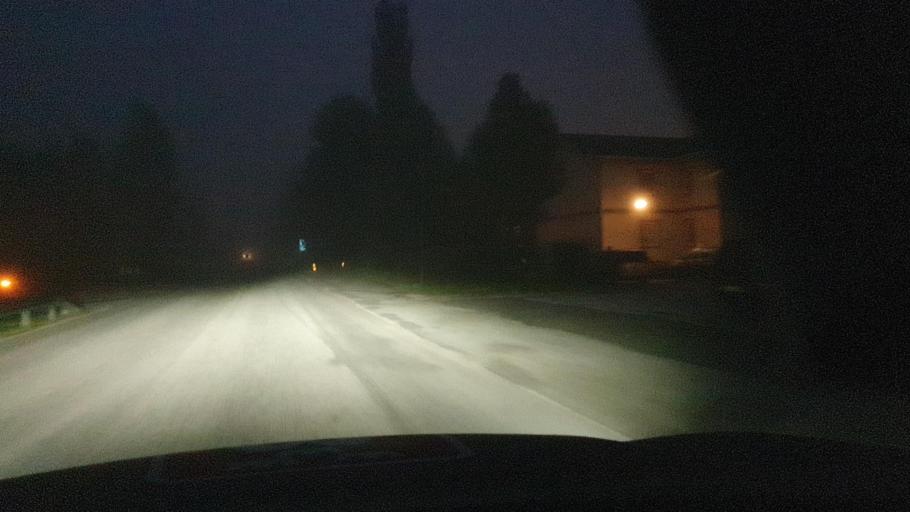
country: SE
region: Vaesternorrland
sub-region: OErnskoeldsviks Kommun
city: Bjasta
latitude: 63.2869
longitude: 18.5630
